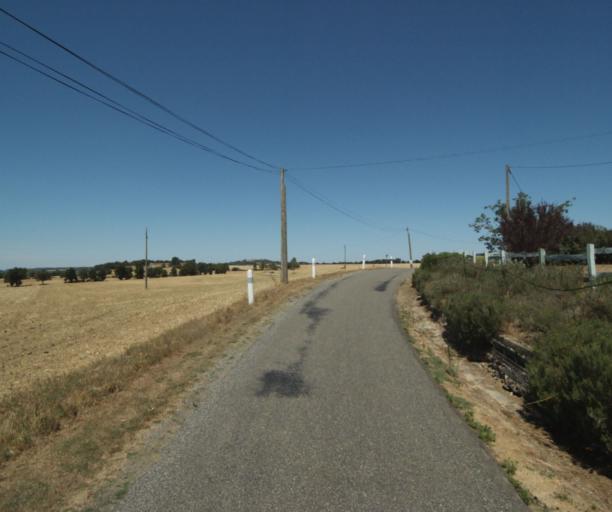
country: FR
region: Midi-Pyrenees
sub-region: Departement de la Haute-Garonne
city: Saint-Felix-Lauragais
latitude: 43.4623
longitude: 1.9049
